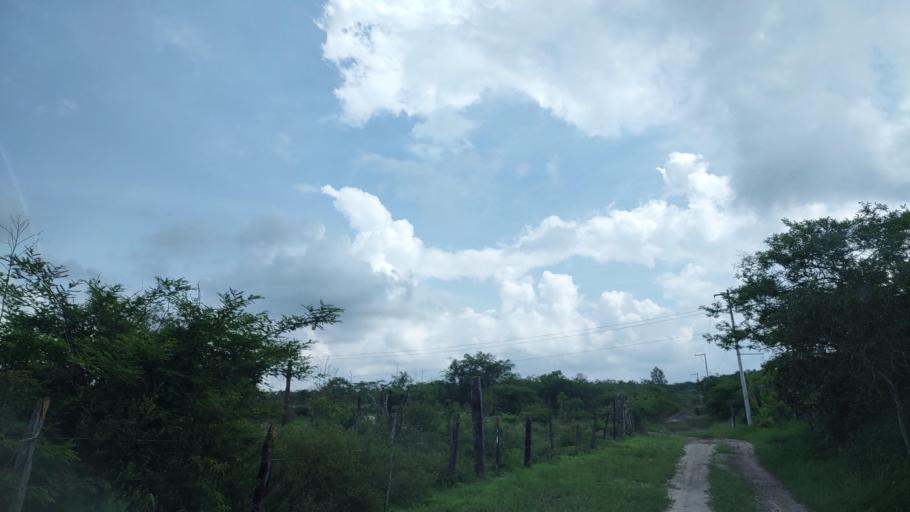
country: MX
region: Veracruz
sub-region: Emiliano Zapata
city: Dos Rios
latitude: 19.4503
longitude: -96.8093
